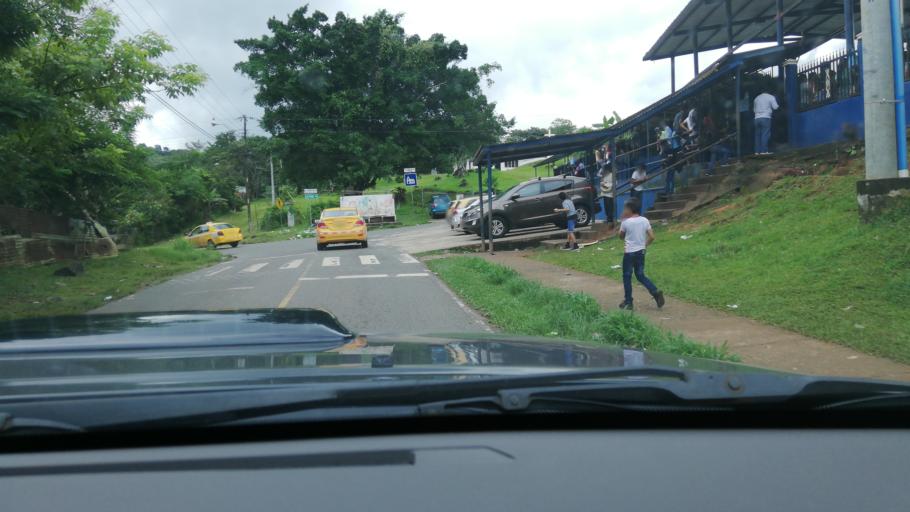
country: PA
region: Panama
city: Cerro Azul
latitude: 9.1104
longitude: -79.4434
